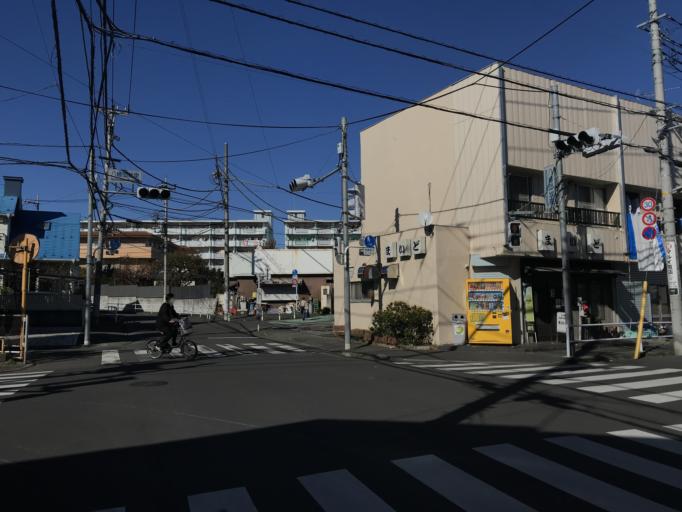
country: JP
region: Tokyo
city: Tanashicho
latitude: 35.7558
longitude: 139.5123
